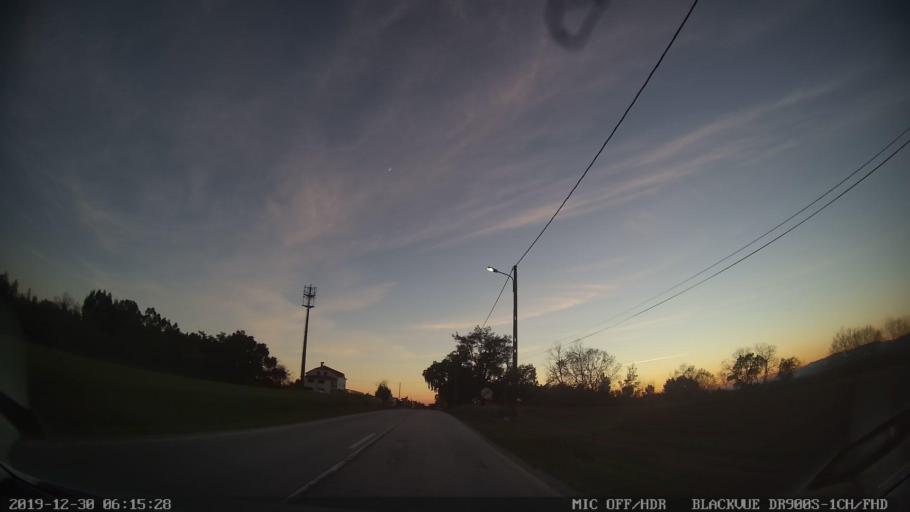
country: PT
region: Castelo Branco
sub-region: Penamacor
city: Penamacor
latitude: 40.1105
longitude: -7.2225
